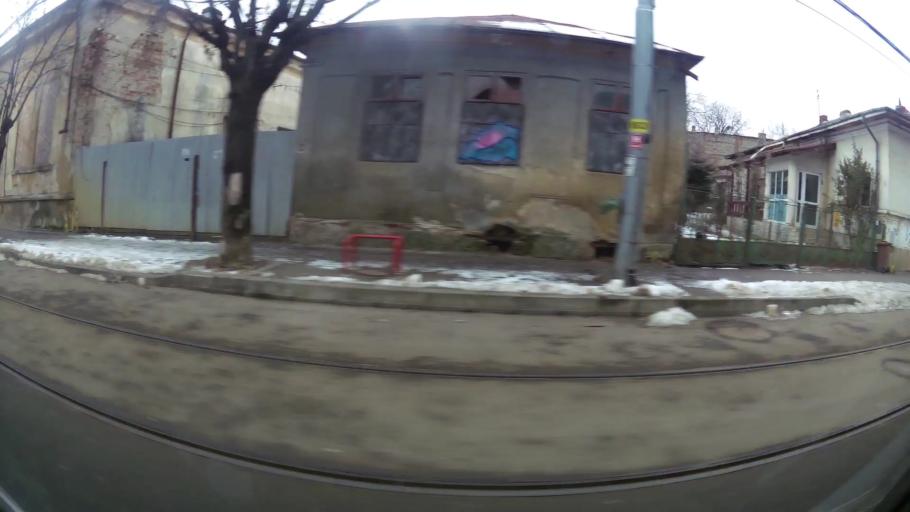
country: RO
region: Prahova
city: Ploiesti
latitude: 44.9374
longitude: 26.0288
